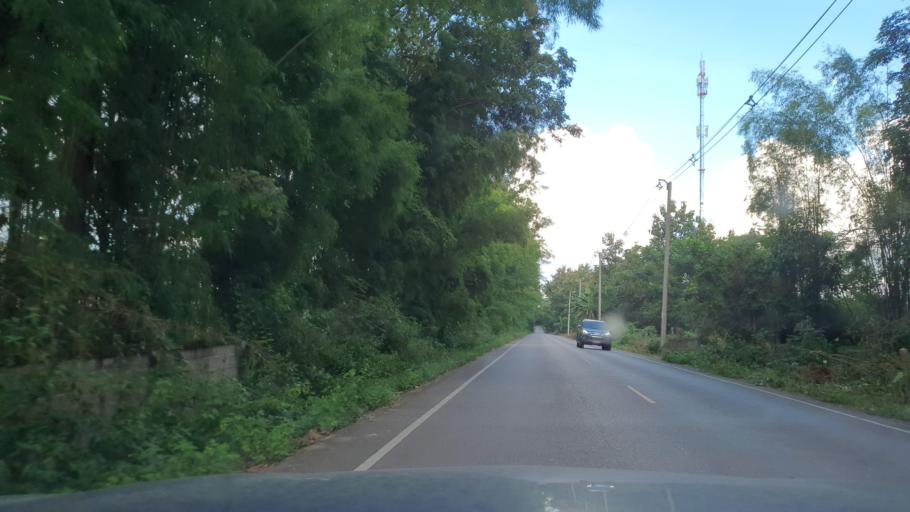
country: TH
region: Phayao
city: Phayao
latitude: 19.0929
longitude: 99.8287
